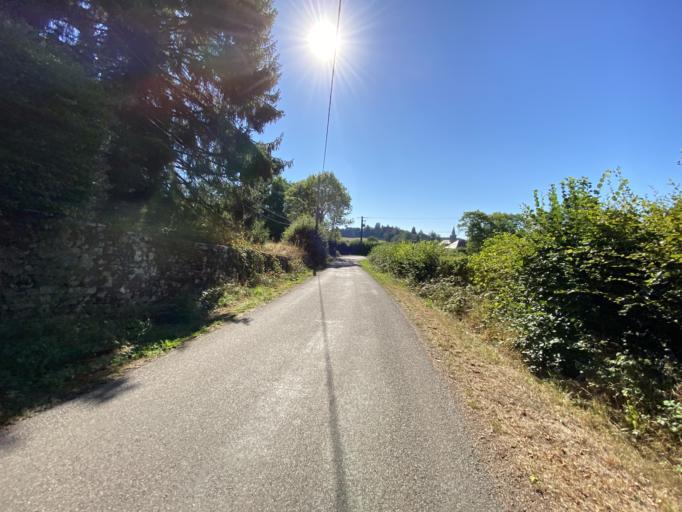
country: FR
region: Bourgogne
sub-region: Departement de la Cote-d'Or
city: Saulieu
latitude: 47.2629
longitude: 4.1761
